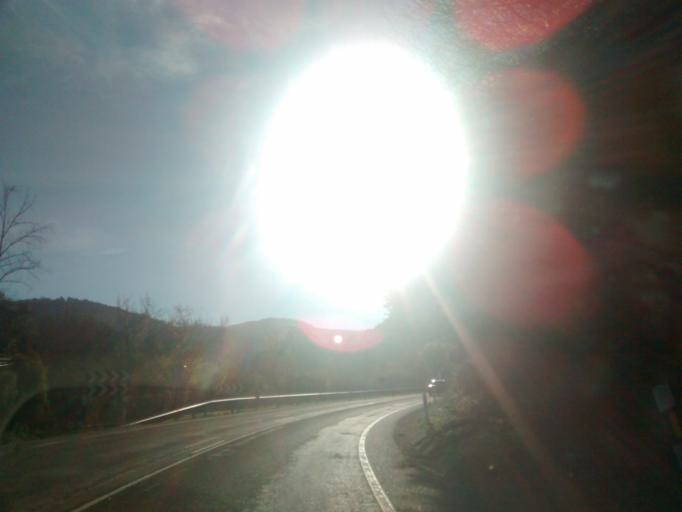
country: ES
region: Cantabria
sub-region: Provincia de Cantabria
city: Santiurde de Toranzo
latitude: 43.1730
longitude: -3.9009
